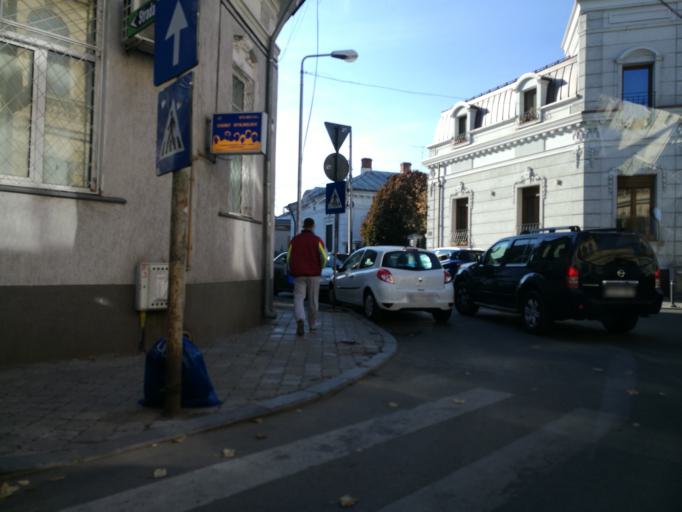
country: RO
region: Bucuresti
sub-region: Municipiul Bucuresti
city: Bucharest
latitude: 44.4448
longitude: 26.1175
